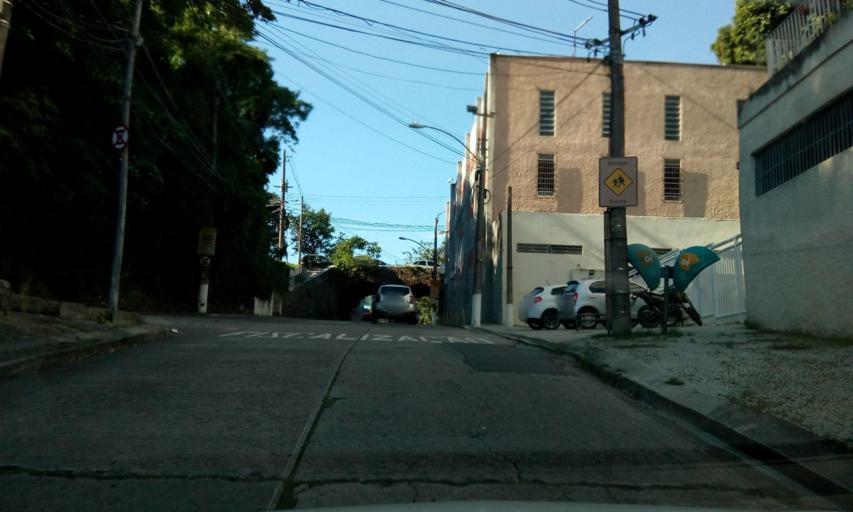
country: BR
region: Rio de Janeiro
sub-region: Rio De Janeiro
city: Rio de Janeiro
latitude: -22.9604
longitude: -43.1787
